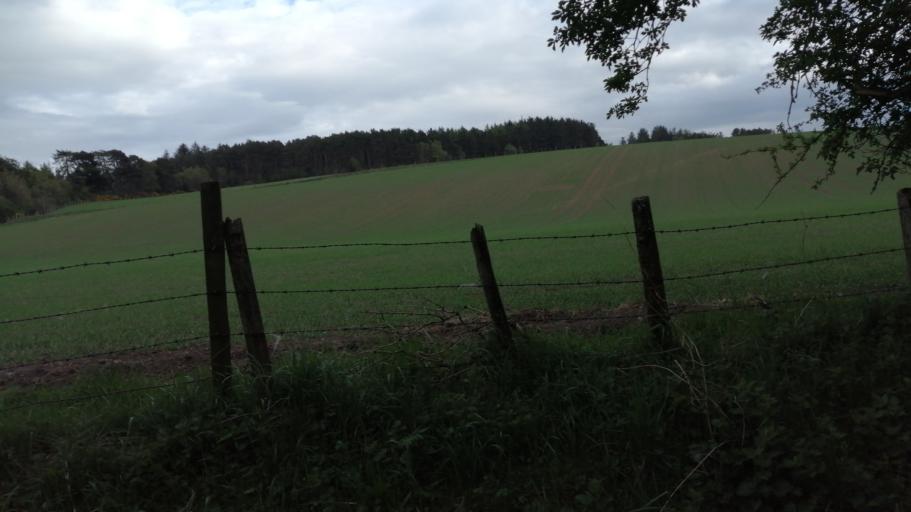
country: GB
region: Scotland
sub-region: Moray
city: Keith
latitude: 57.5367
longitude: -2.9300
